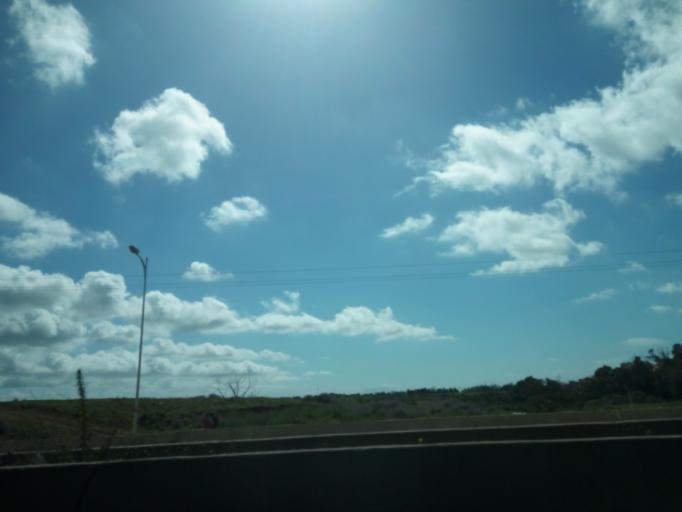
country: DZ
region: Tipaza
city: Cheraga
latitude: 36.7318
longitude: 2.9345
